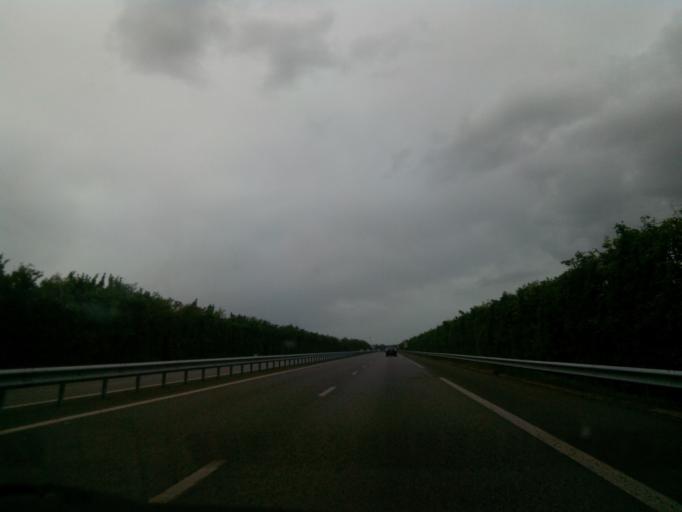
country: FR
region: Brittany
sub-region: Departement d'Ille-et-Vilaine
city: Plelan-le-Grand
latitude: 47.9807
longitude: -2.0978
